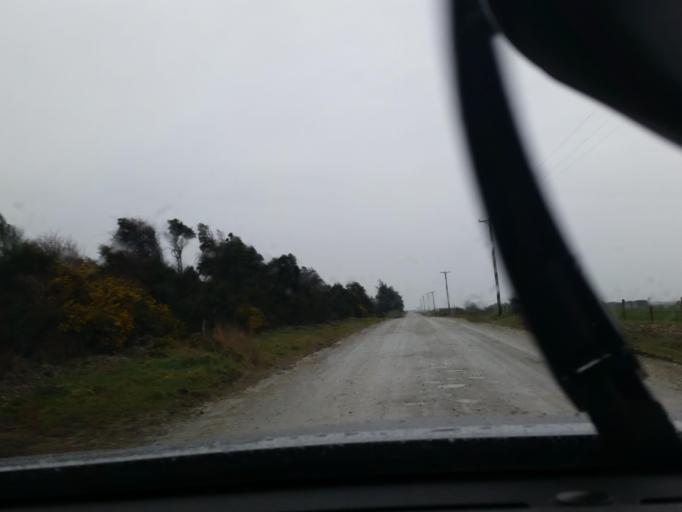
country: NZ
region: Southland
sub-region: Invercargill City
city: Invercargill
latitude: -46.4273
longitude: 168.5062
